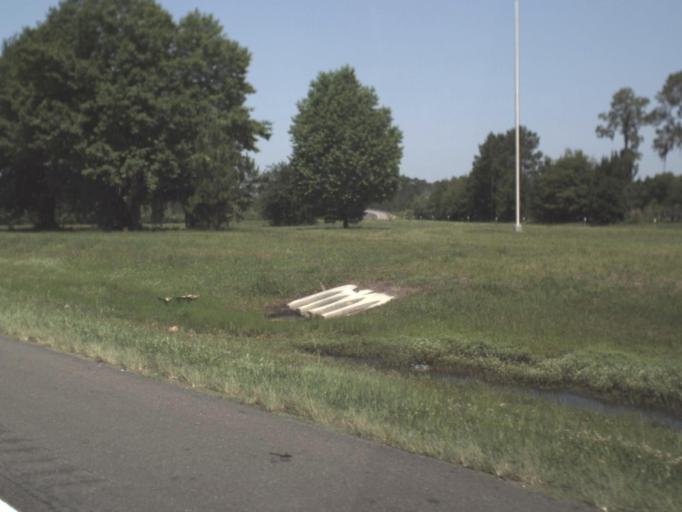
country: US
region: Florida
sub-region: Duval County
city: Baldwin
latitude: 30.3076
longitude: -81.8703
